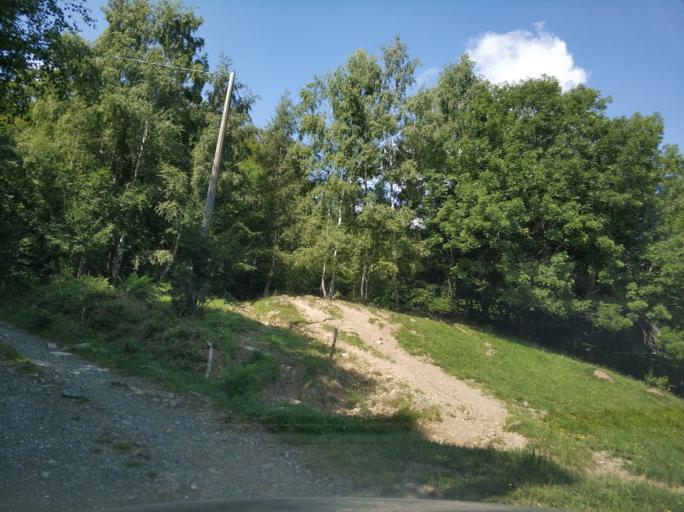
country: IT
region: Piedmont
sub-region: Provincia di Torino
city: Viu
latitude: 45.1980
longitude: 7.3668
